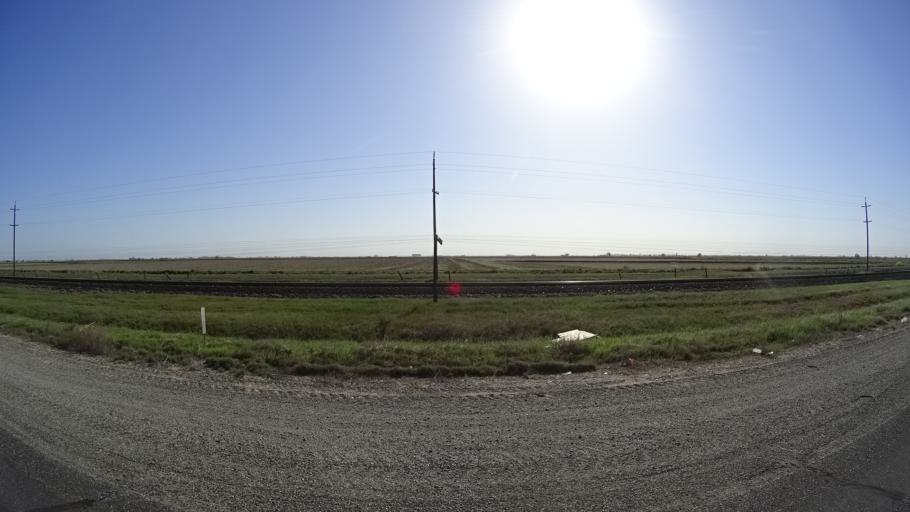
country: US
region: California
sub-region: Glenn County
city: Willows
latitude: 39.4723
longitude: -122.1930
